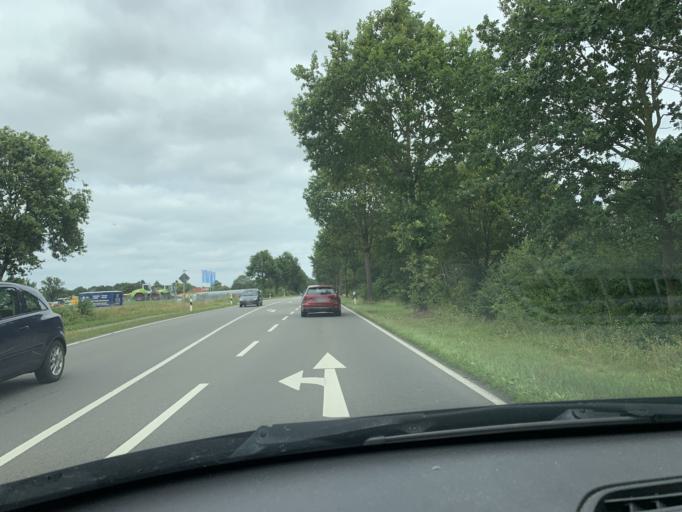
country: DE
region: Lower Saxony
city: Westerstede
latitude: 53.2704
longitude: 7.9519
